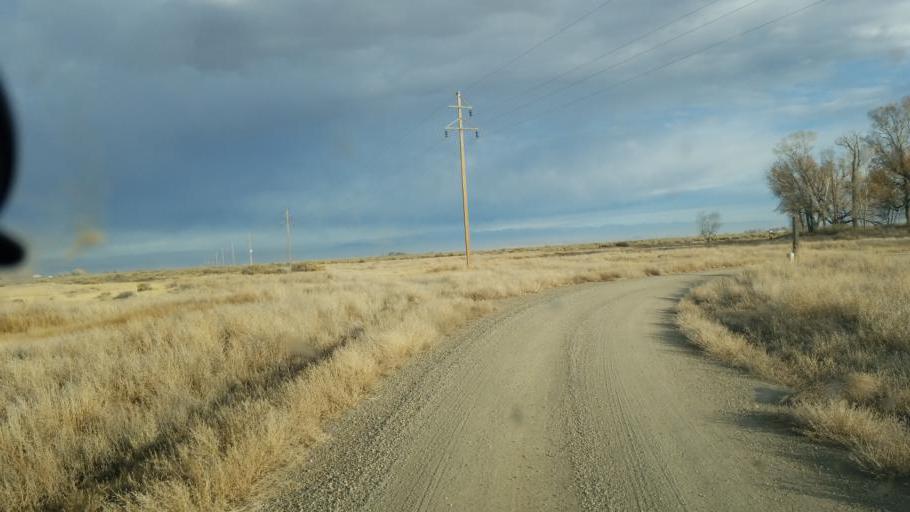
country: US
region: Colorado
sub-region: Alamosa County
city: Alamosa East
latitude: 37.4592
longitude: -105.8330
